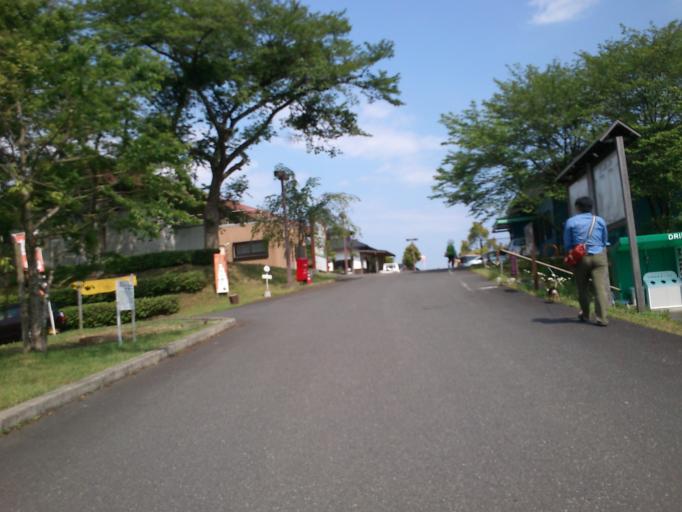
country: JP
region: Kyoto
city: Fukuchiyama
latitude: 35.3386
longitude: 134.9293
